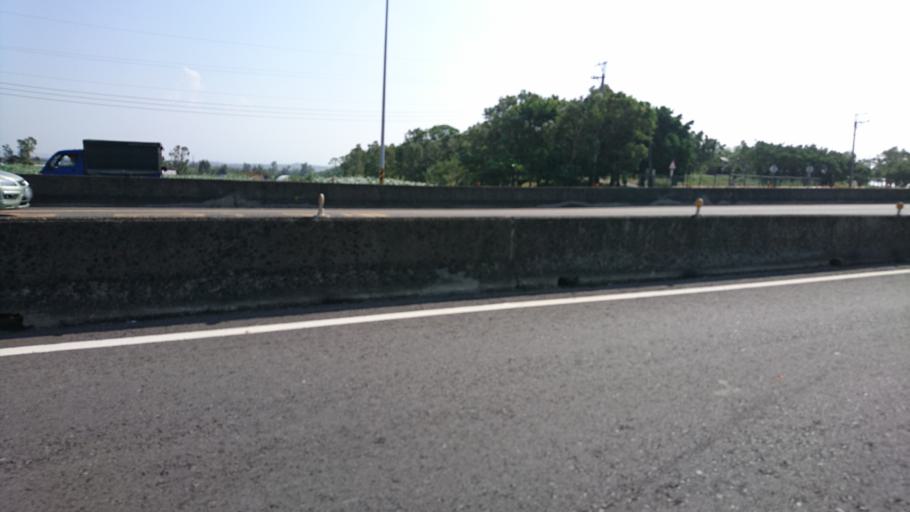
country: TW
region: Taiwan
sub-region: Miaoli
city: Miaoli
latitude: 24.6732
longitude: 120.8387
